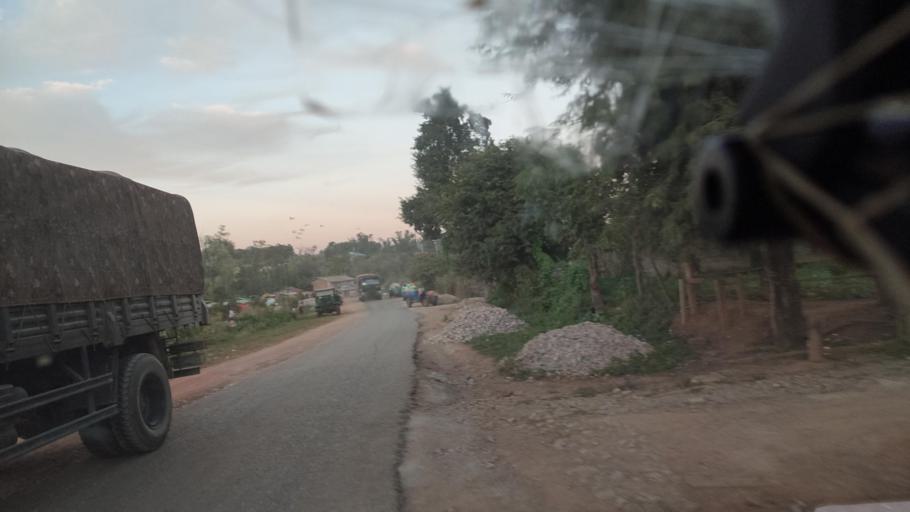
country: MM
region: Shan
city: Taunggyi
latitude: 20.9998
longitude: 97.9515
